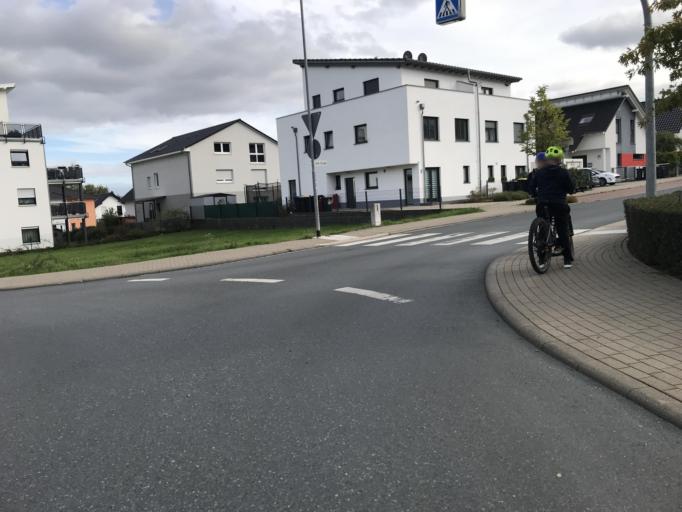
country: DE
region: Hesse
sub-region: Regierungsbezirk Darmstadt
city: Butzbach
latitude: 50.4407
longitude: 8.6548
